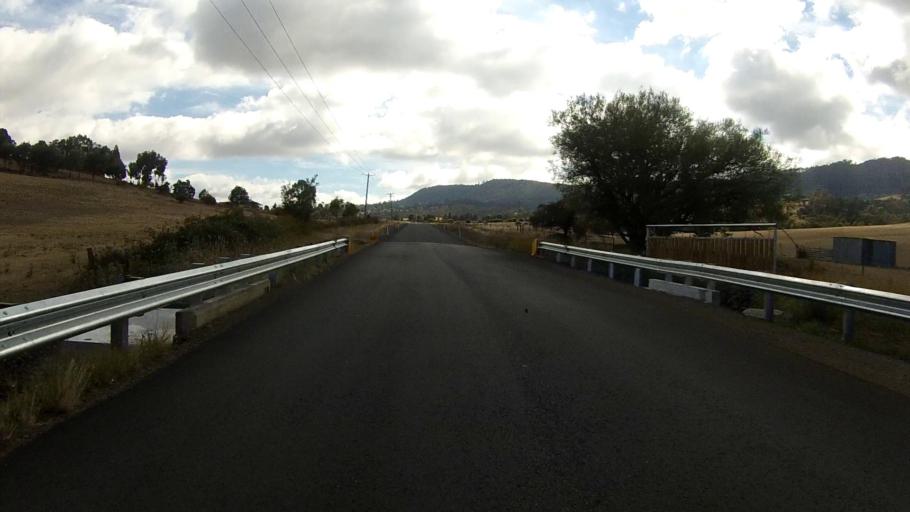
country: AU
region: Tasmania
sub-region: Brighton
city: Old Beach
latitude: -42.7676
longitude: 147.2974
